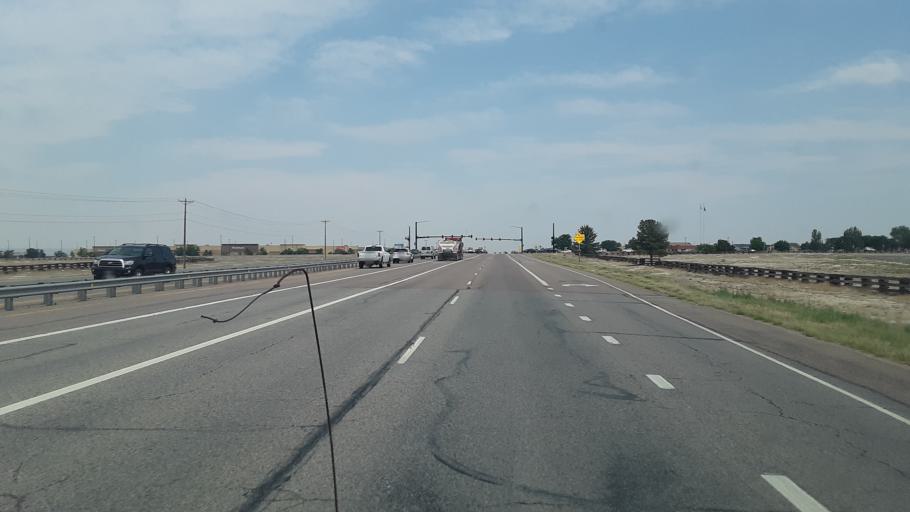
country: US
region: Colorado
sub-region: Pueblo County
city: Pueblo West
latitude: 38.3365
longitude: -104.7473
